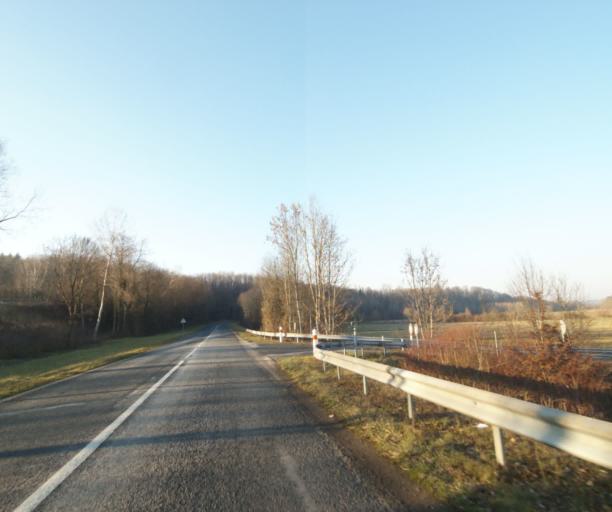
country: FR
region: Champagne-Ardenne
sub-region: Departement de la Haute-Marne
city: Bienville
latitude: 48.5683
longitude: 5.0405
